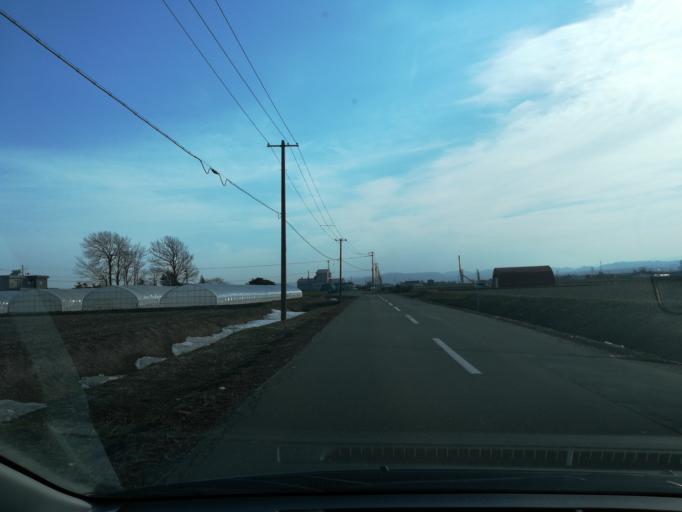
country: JP
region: Hokkaido
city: Iwamizawa
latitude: 43.1914
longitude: 141.7091
